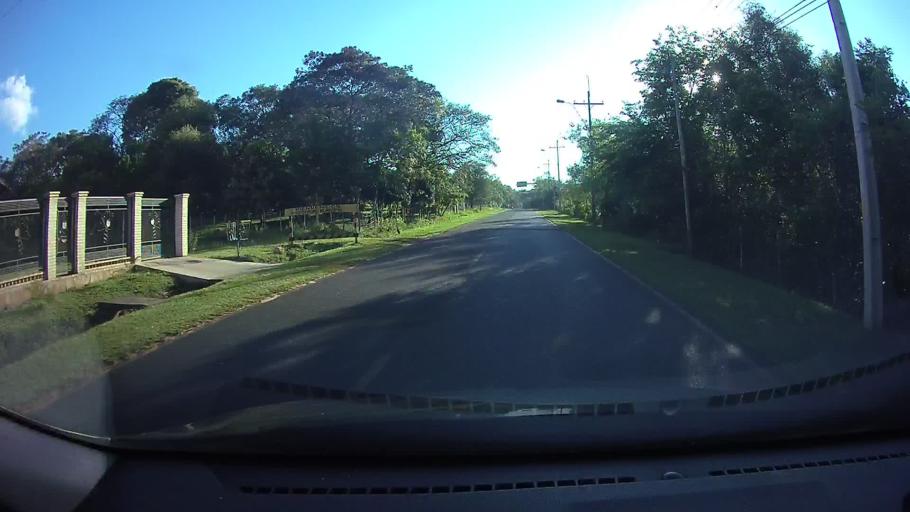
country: PY
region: Cordillera
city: Emboscada
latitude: -25.1925
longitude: -57.3124
